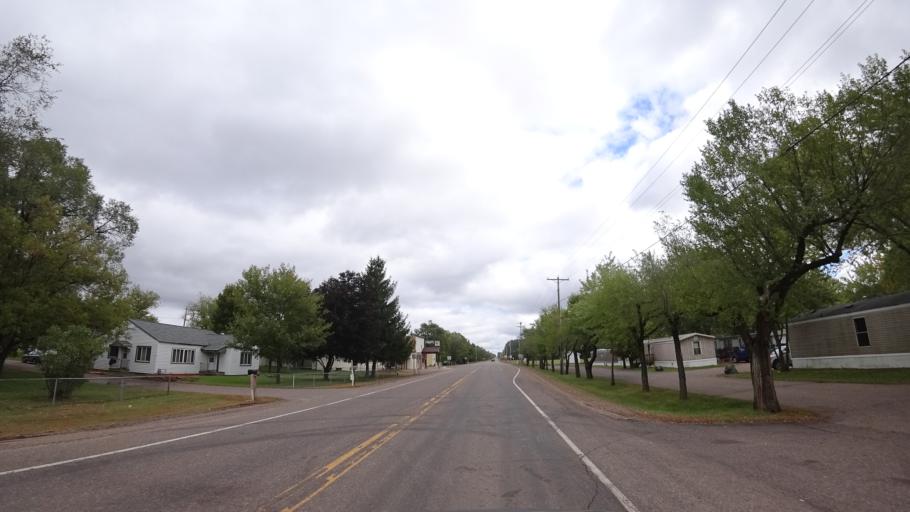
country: US
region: Wisconsin
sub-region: Chippewa County
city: Lake Wissota
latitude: 44.9296
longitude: -91.2691
